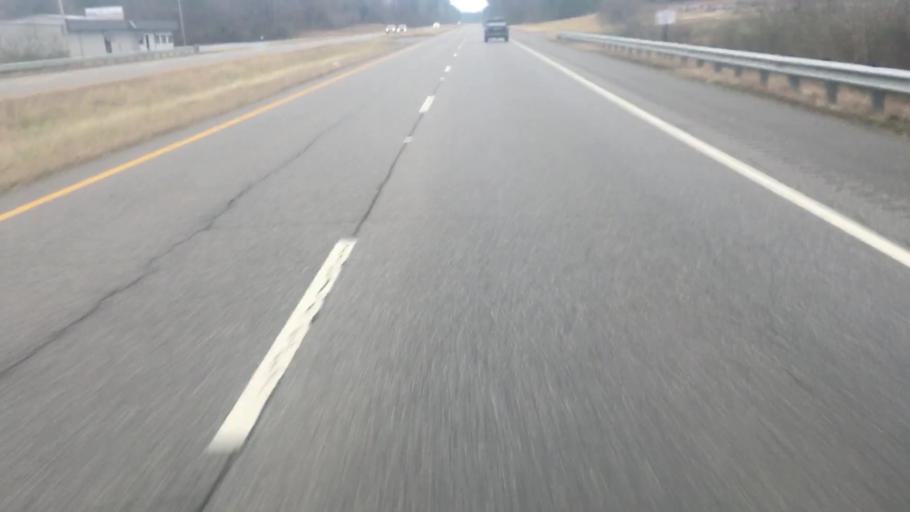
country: US
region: Alabama
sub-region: Walker County
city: Jasper
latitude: 33.8297
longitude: -87.2078
